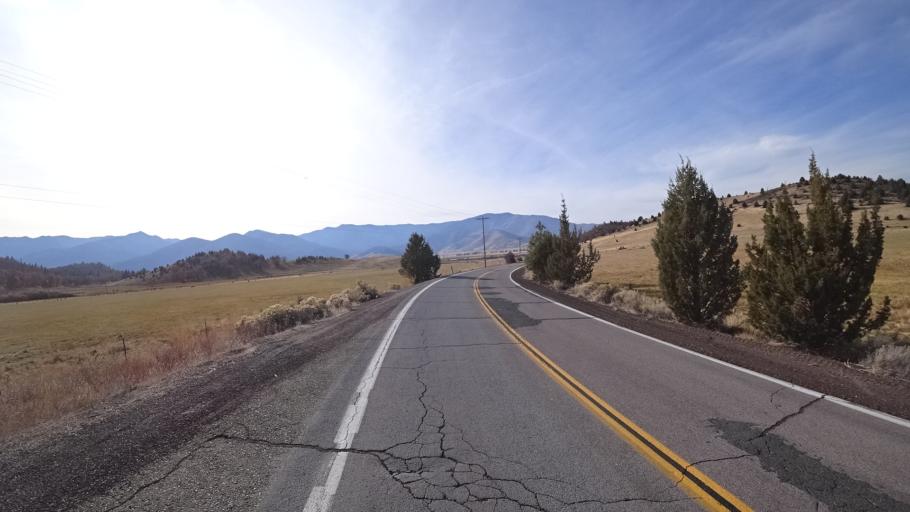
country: US
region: California
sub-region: Siskiyou County
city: Weed
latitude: 41.4680
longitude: -122.4151
